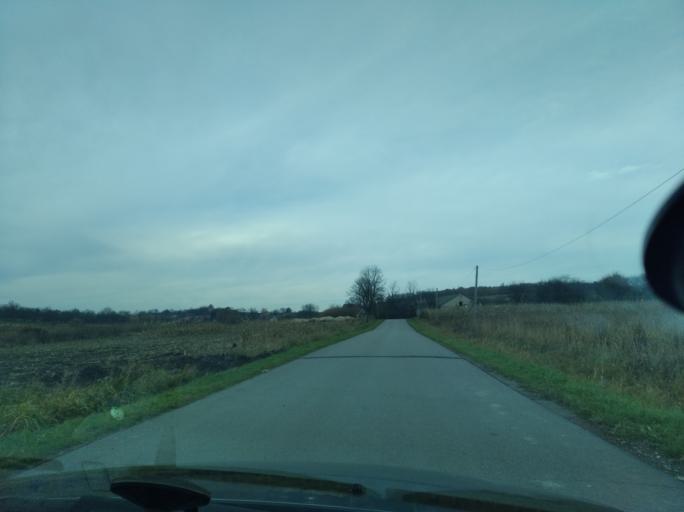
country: PL
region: Subcarpathian Voivodeship
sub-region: Powiat przeworski
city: Debow
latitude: 50.0485
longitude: 22.4232
